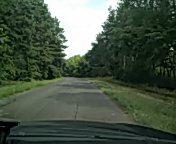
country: HU
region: Hajdu-Bihar
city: Hosszupalyi
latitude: 47.4942
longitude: 21.7279
